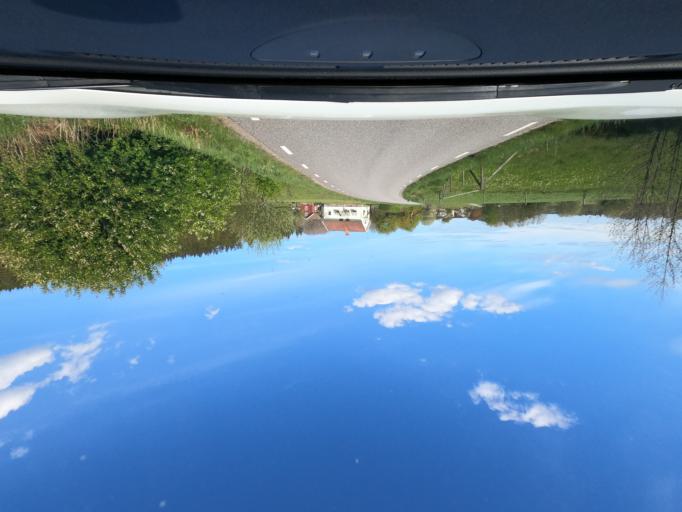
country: SE
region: Vaestra Goetaland
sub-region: Harryda Kommun
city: Ravlanda
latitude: 57.6196
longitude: 12.4965
